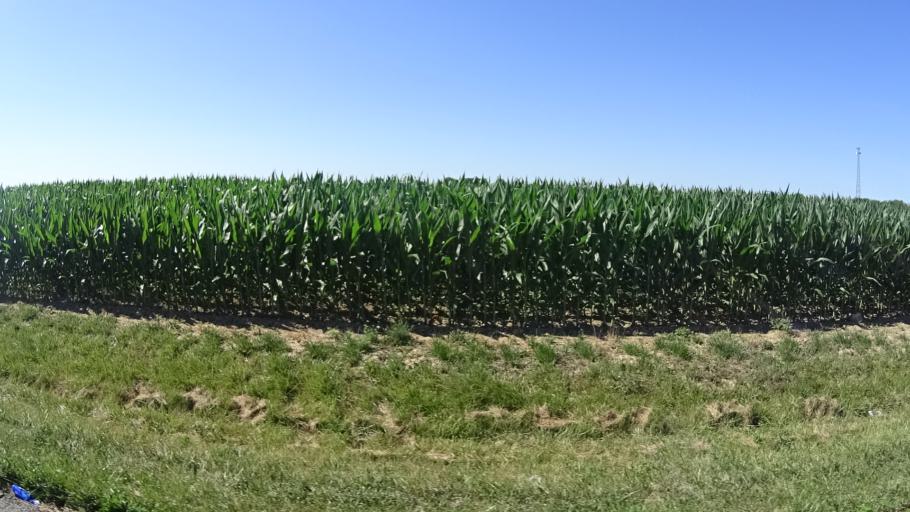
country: US
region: Ohio
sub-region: Erie County
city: Sandusky
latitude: 41.4093
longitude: -82.7224
